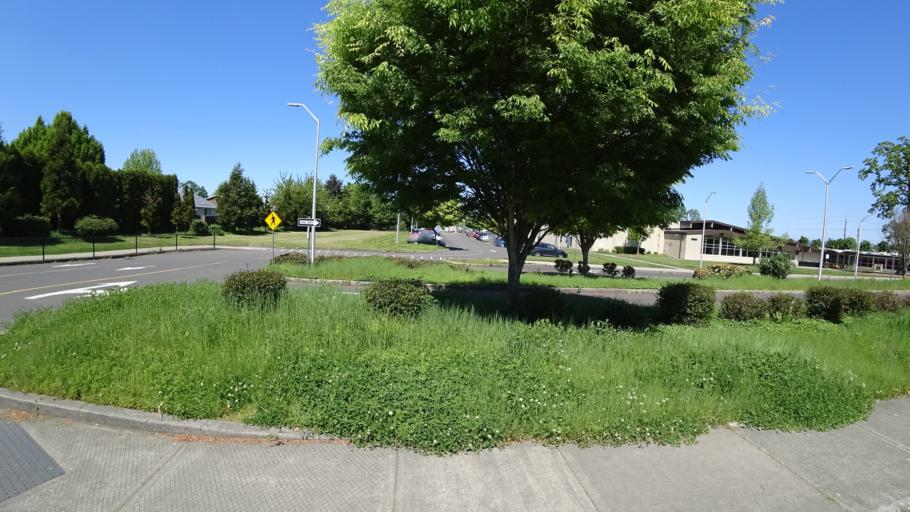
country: US
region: Oregon
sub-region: Washington County
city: Aloha
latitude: 45.5087
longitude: -122.9043
